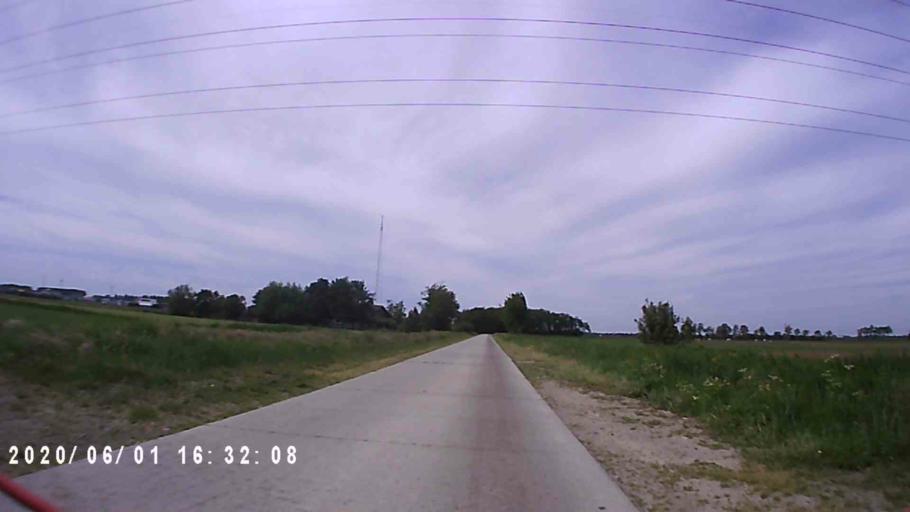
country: NL
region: Friesland
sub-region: Gemeente Leeuwarden
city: Camminghaburen
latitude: 53.1887
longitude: 5.8650
